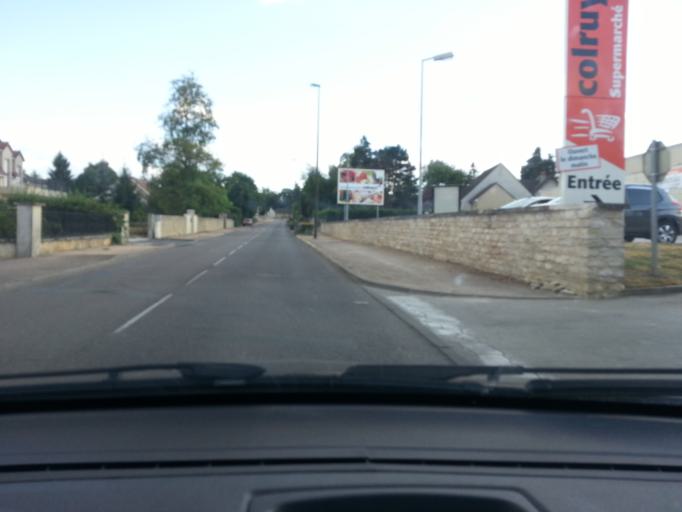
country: FR
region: Bourgogne
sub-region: Departement de Saone-et-Loire
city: Givry
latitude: 46.7768
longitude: 4.7390
